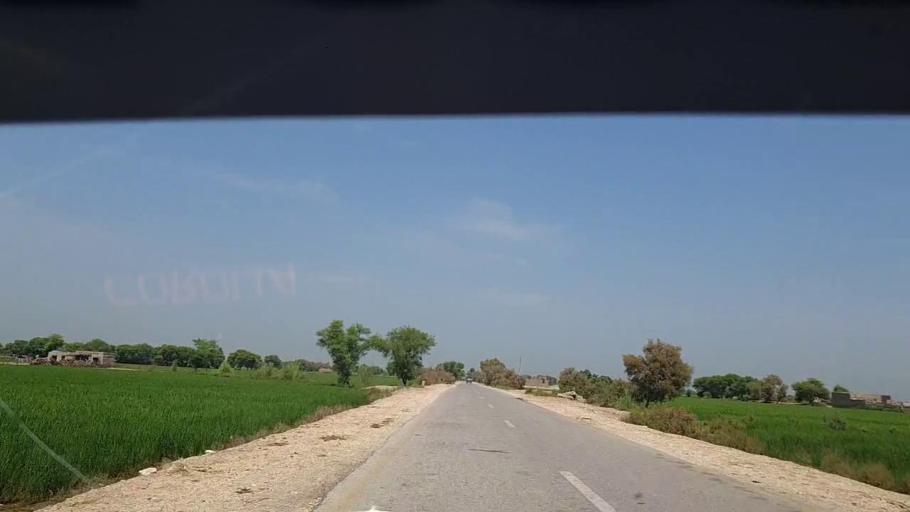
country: PK
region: Sindh
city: Thul
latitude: 28.1439
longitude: 68.8177
